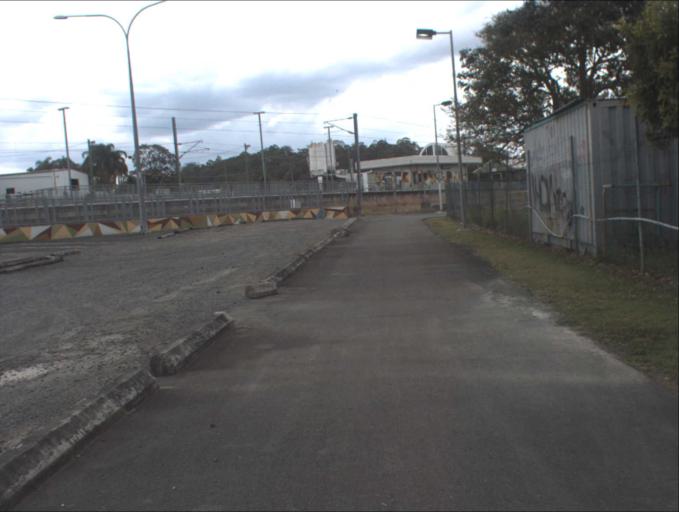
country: AU
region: Queensland
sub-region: Logan
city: Beenleigh
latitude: -27.7097
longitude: 153.1884
